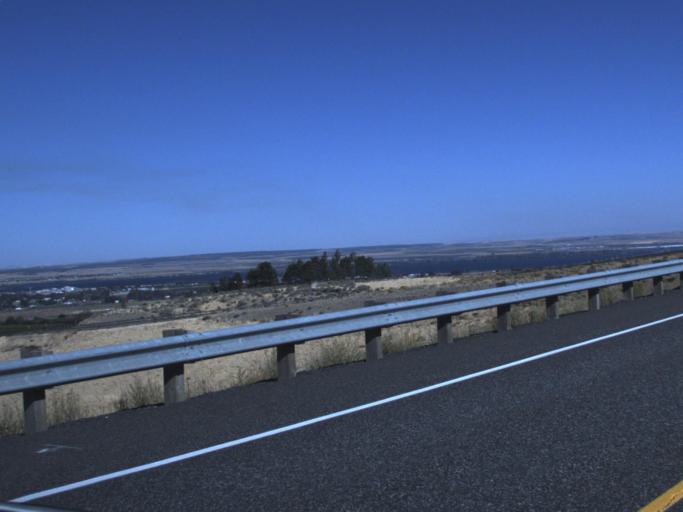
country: US
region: Washington
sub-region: Benton County
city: Highland
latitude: 46.1277
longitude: -119.0708
